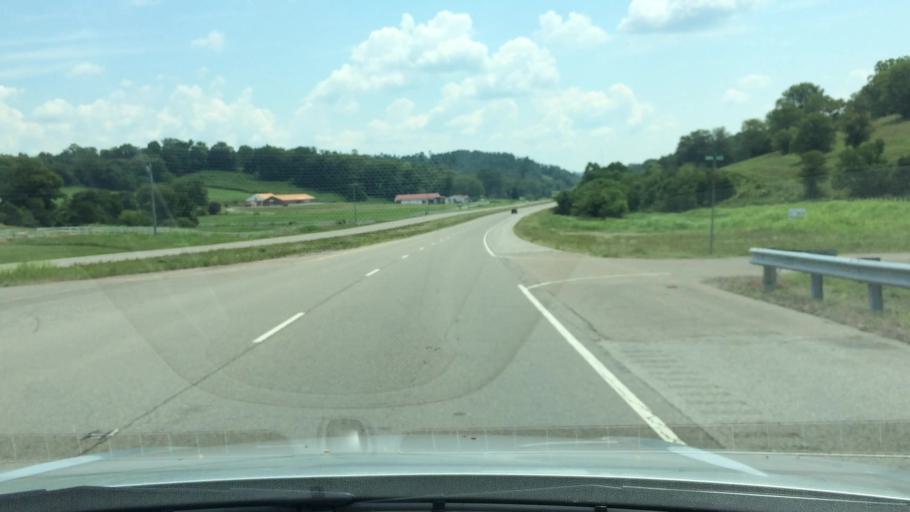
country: US
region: Tennessee
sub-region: Giles County
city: Pulaski
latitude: 35.1774
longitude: -86.9826
